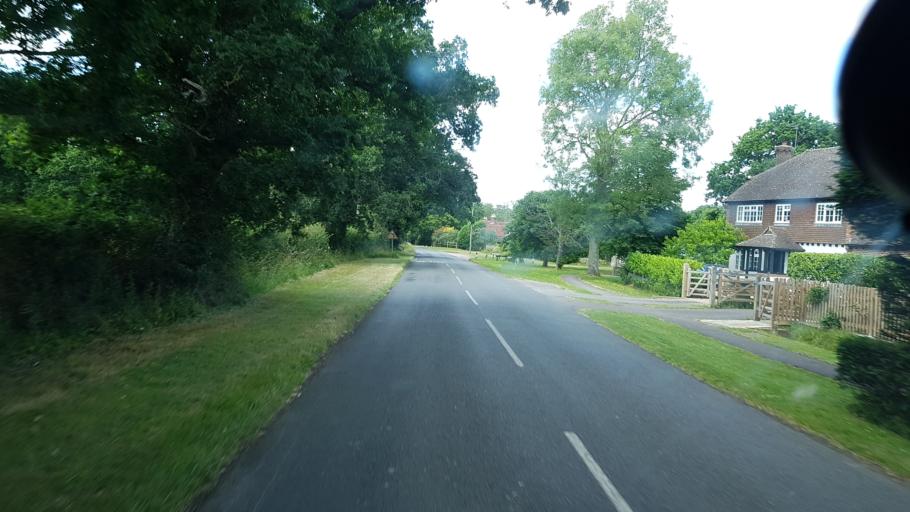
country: GB
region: England
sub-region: West Sussex
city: Rudgwick
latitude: 51.0803
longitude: -0.4534
